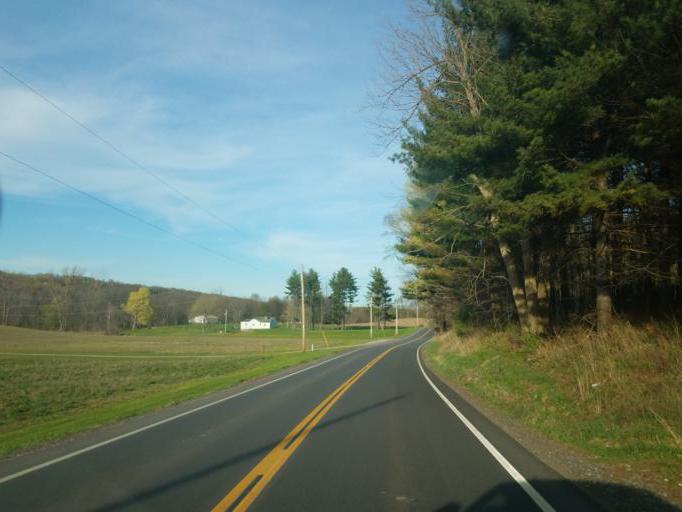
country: US
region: Ohio
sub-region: Richland County
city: Lexington
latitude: 40.7039
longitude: -82.6764
